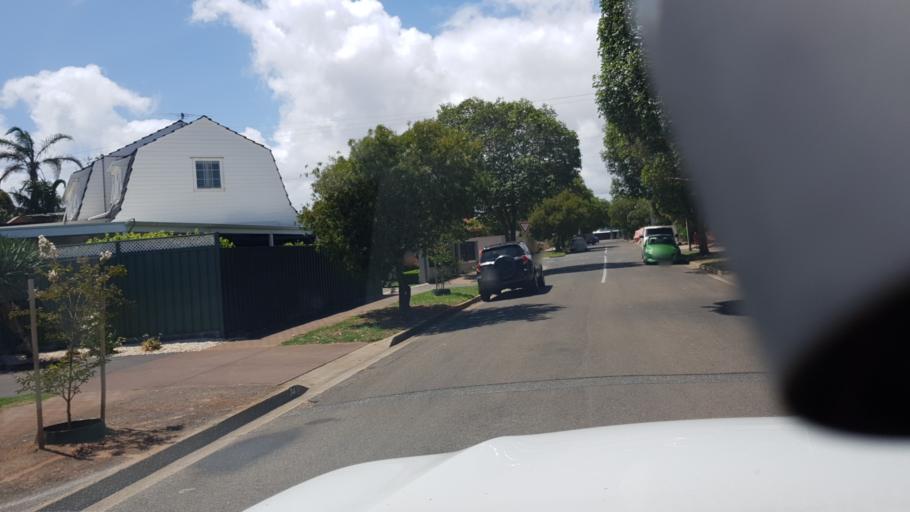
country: AU
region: South Australia
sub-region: Holdfast Bay
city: North Brighton
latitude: -35.0048
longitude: 138.5262
